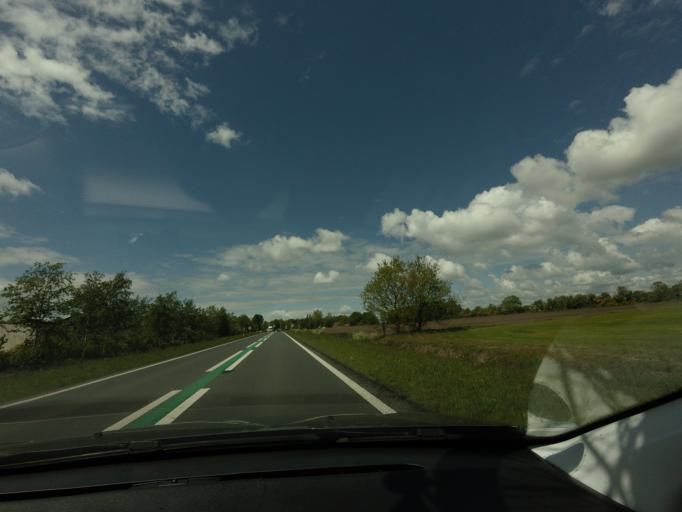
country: NL
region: Friesland
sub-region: Gemeente Gaasterlan-Sleat
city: Balk
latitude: 52.8777
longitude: 5.6137
